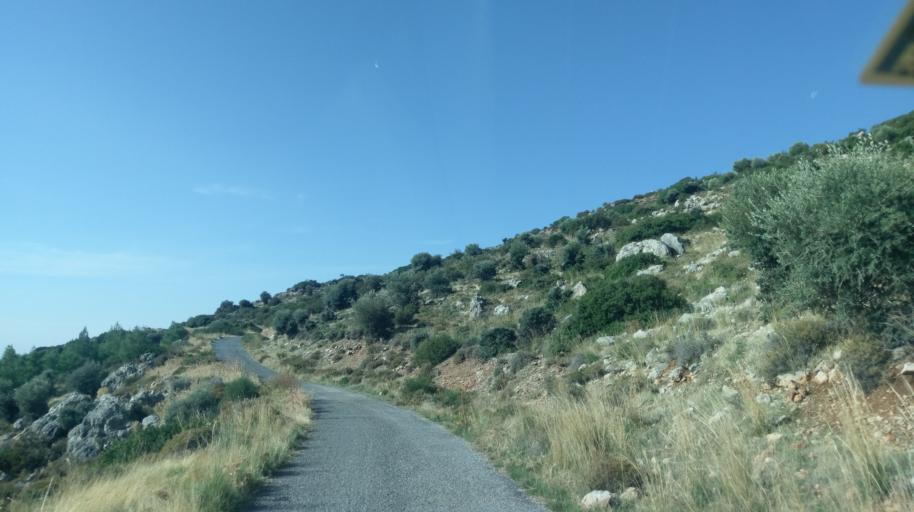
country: CY
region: Keryneia
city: Kyrenia
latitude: 35.2843
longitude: 33.4086
